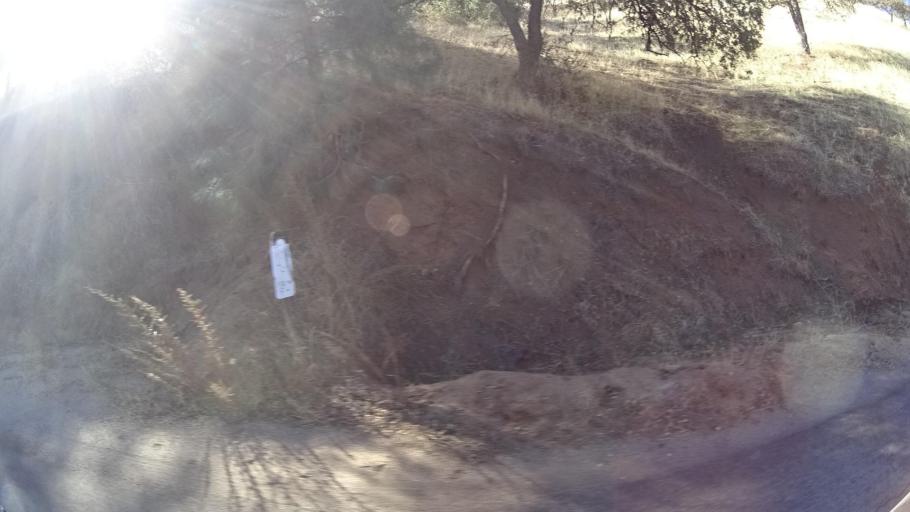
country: US
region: California
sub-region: Kern County
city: Bear Valley Springs
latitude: 35.3475
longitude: -118.5723
